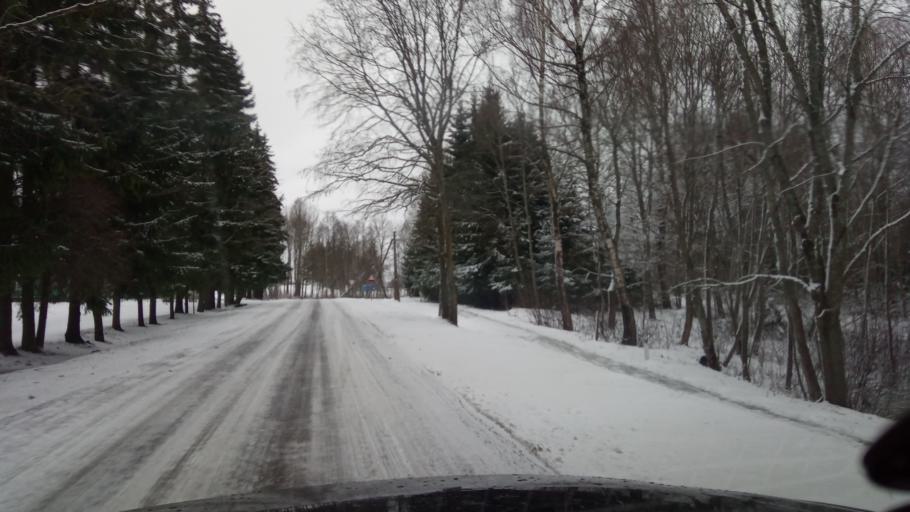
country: LT
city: Zarasai
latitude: 55.6293
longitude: 25.9551
